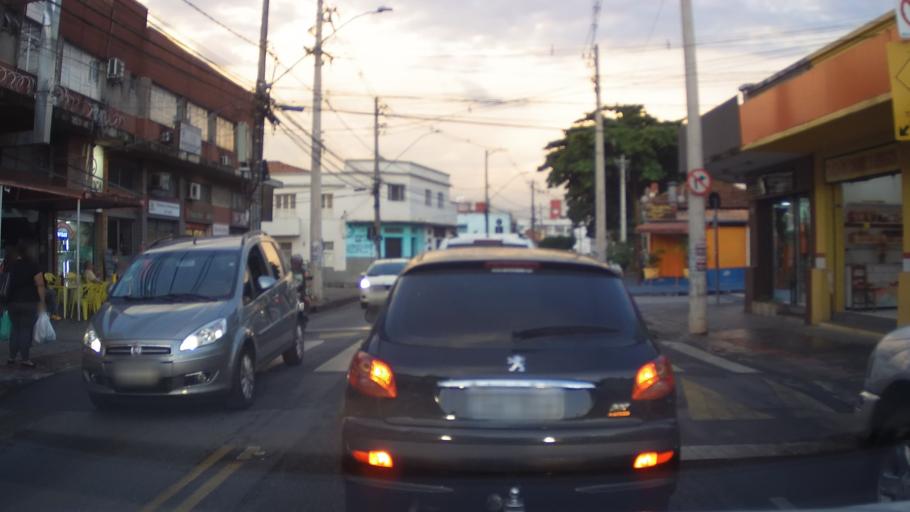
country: BR
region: Minas Gerais
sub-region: Belo Horizonte
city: Belo Horizonte
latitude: -19.9274
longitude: -43.9769
